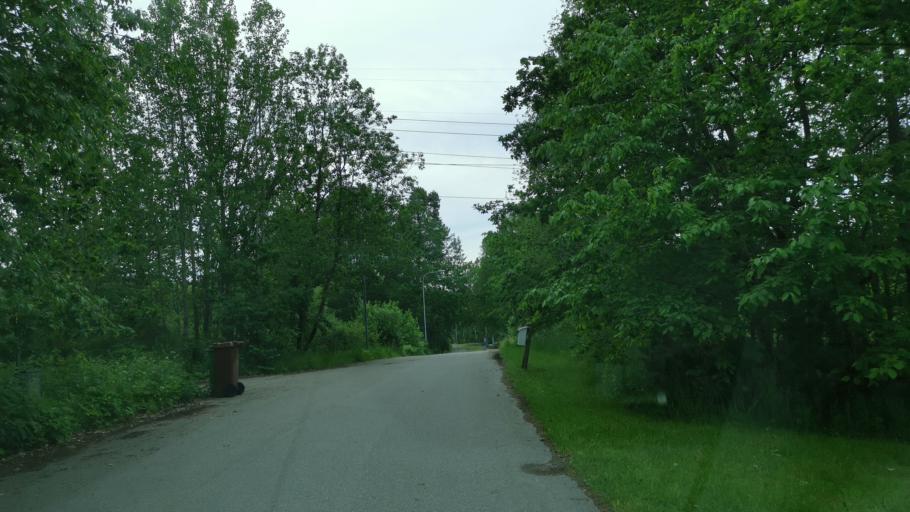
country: SE
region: Vaestra Goetaland
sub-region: Vanersborgs Kommun
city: Vargon
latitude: 58.3571
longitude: 12.3724
